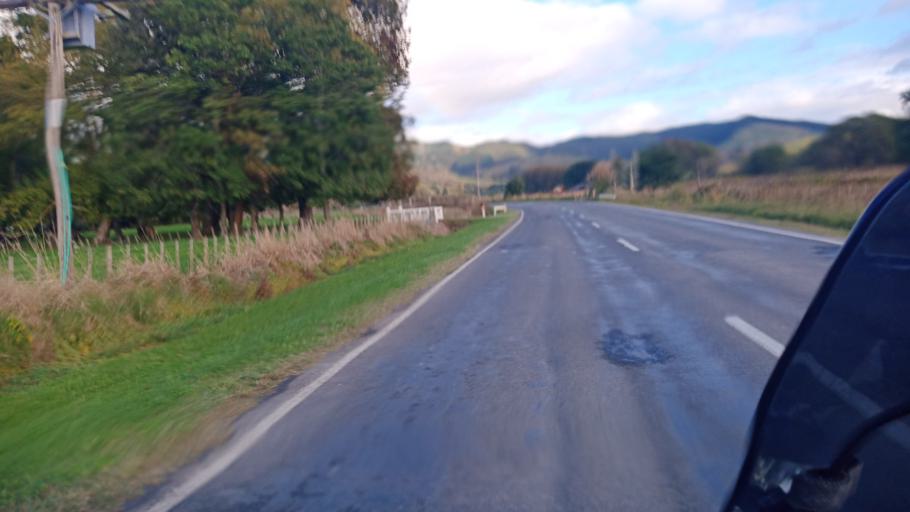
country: NZ
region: Gisborne
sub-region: Gisborne District
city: Gisborne
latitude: -38.6340
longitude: 177.8455
